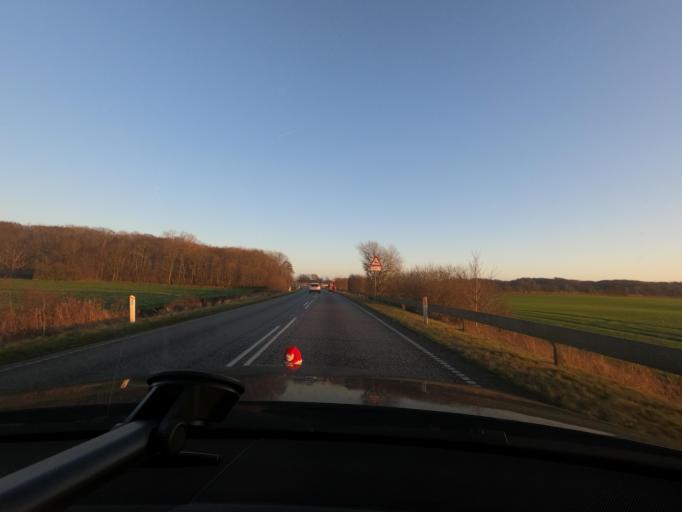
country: DK
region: South Denmark
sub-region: Sonderborg Kommune
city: Horuphav
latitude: 54.9222
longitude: 9.8789
